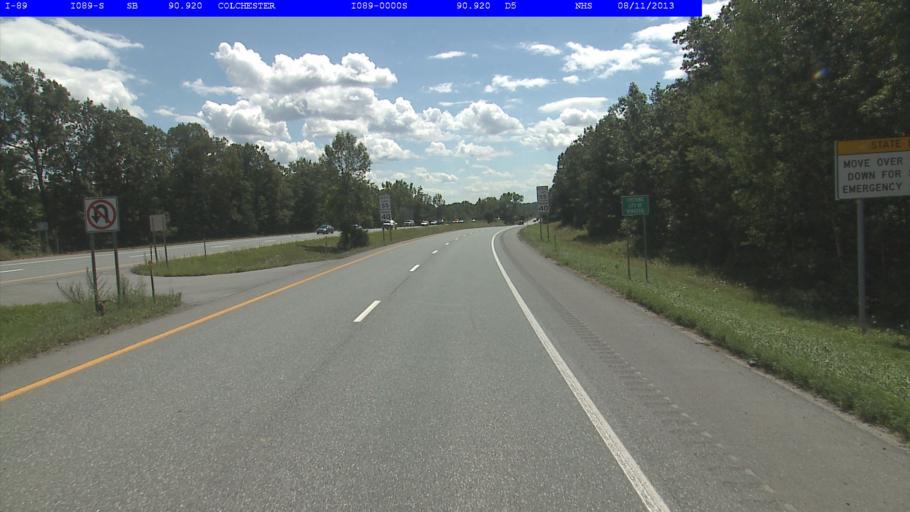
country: US
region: Vermont
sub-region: Chittenden County
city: Winooski
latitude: 44.4997
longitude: -73.1740
